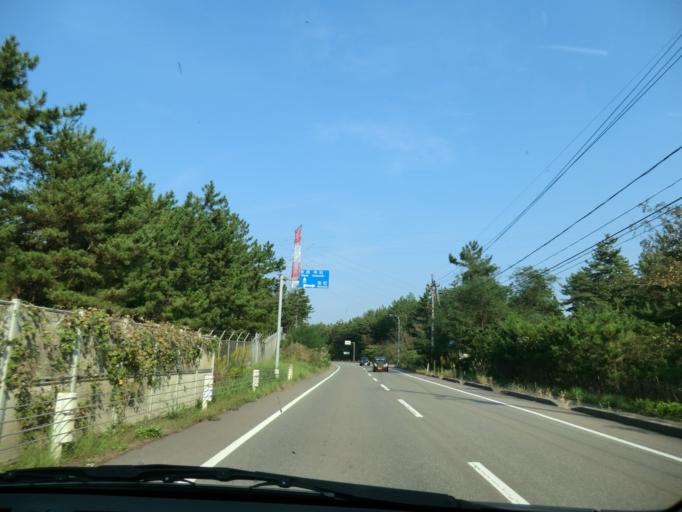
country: JP
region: Niigata
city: Kashiwazaki
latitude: 37.4179
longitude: 138.6001
